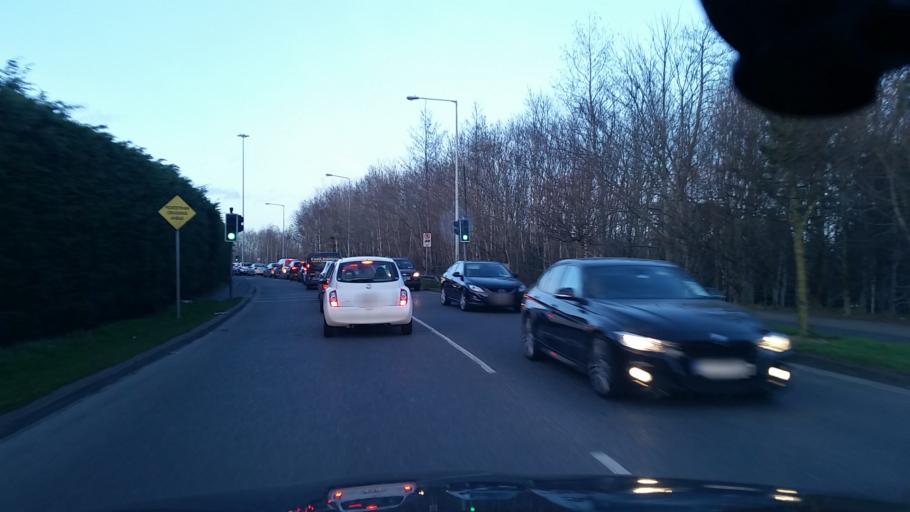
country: IE
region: Leinster
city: Hartstown
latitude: 53.4072
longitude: -6.4291
